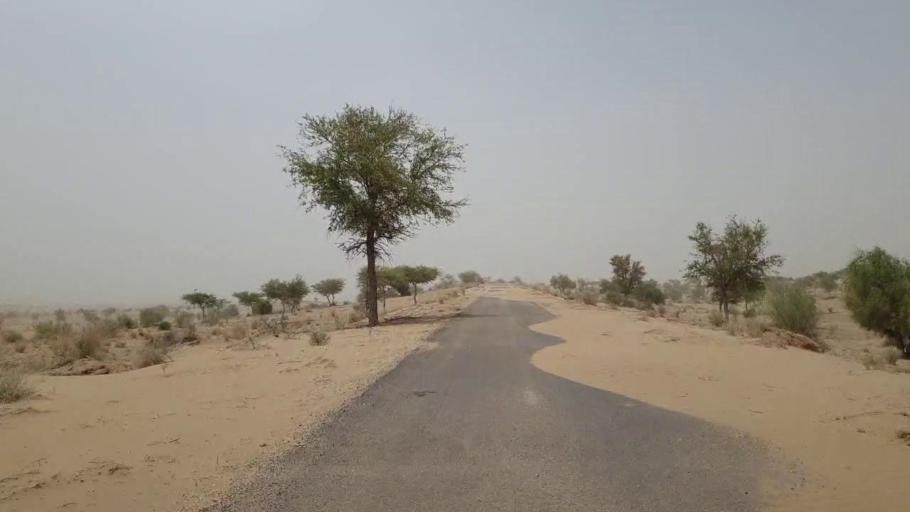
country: PK
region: Sindh
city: Islamkot
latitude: 24.7988
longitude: 70.5182
